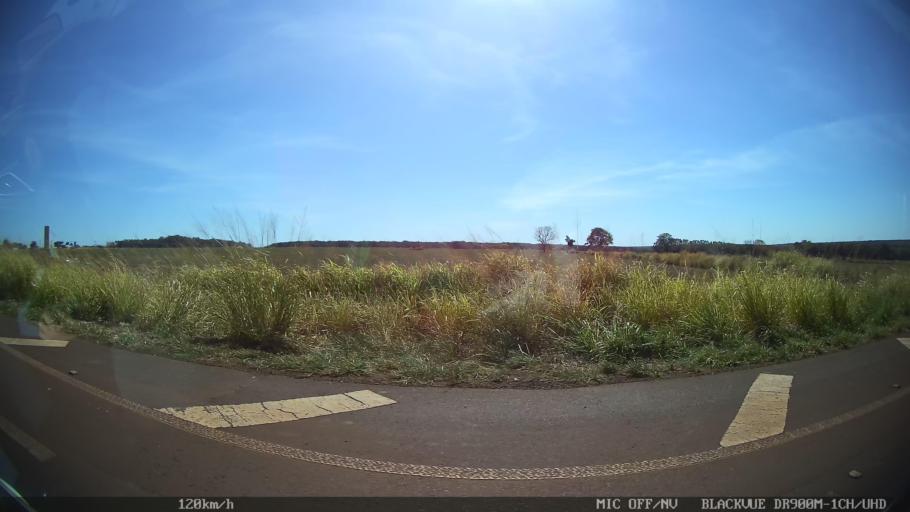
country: BR
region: Sao Paulo
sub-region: Barretos
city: Barretos
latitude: -20.5252
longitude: -48.5868
